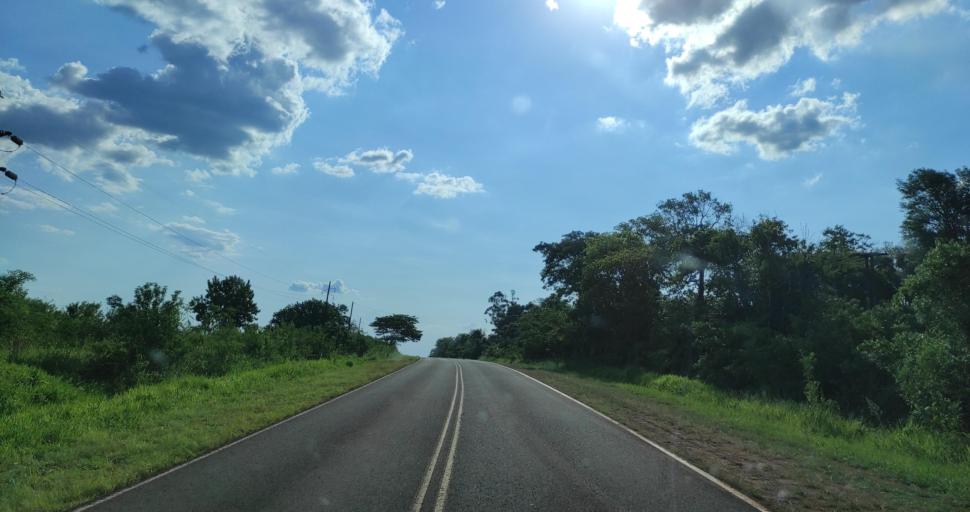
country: AR
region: Misiones
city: San Vicente
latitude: -26.3496
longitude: -54.2036
